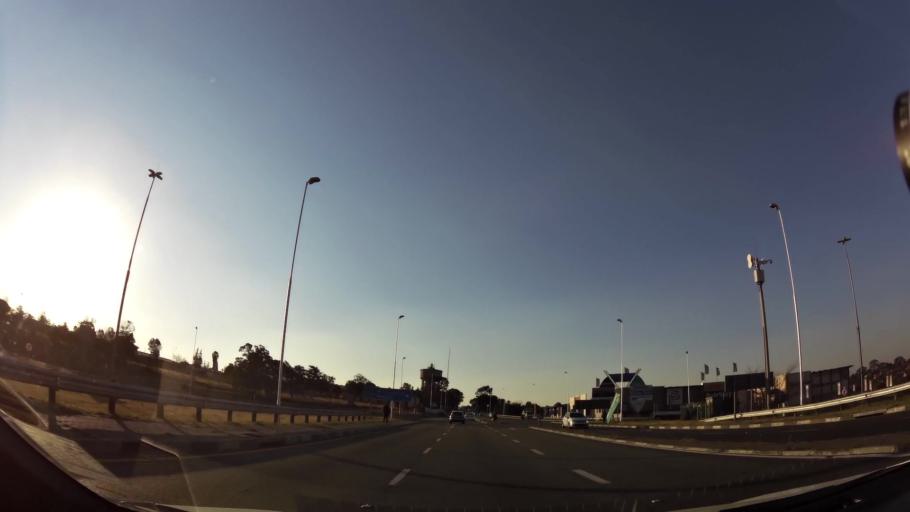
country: ZA
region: Gauteng
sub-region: City of Johannesburg Metropolitan Municipality
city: Johannesburg
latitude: -26.2610
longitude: 28.0077
